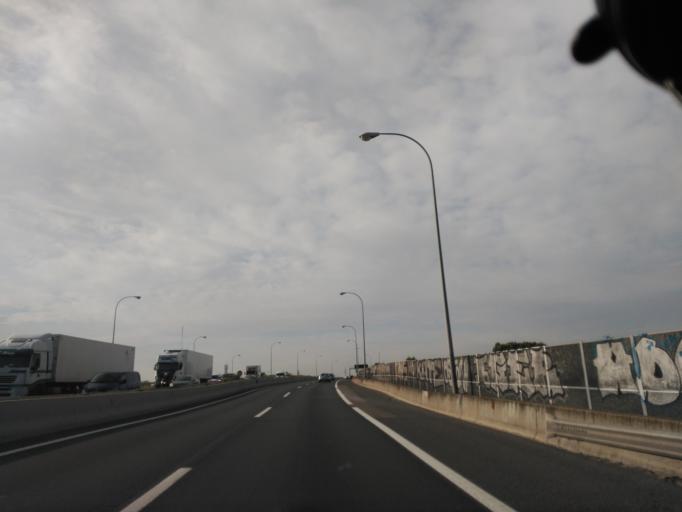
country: ES
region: Madrid
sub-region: Provincia de Madrid
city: Villaverde
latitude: 40.3481
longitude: -3.6737
